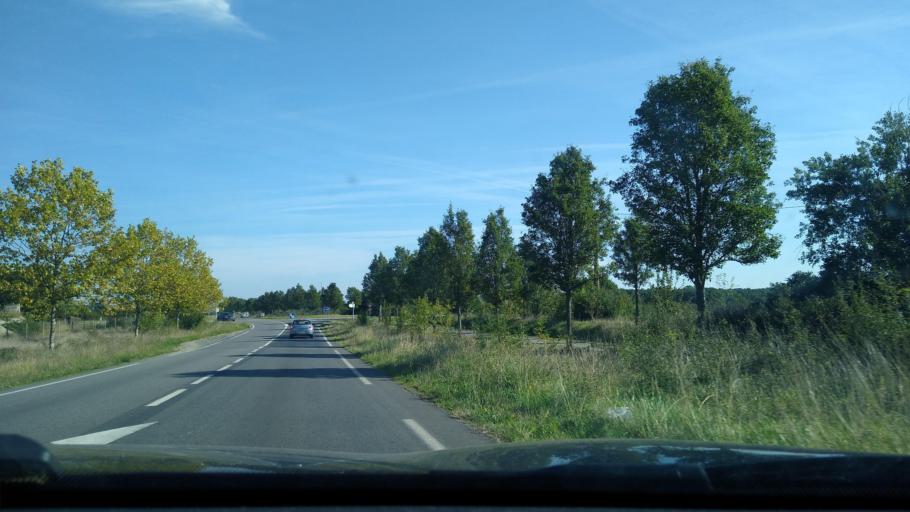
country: FR
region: Midi-Pyrenees
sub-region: Departement de la Haute-Garonne
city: Aussonne
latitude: 43.6667
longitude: 1.3082
